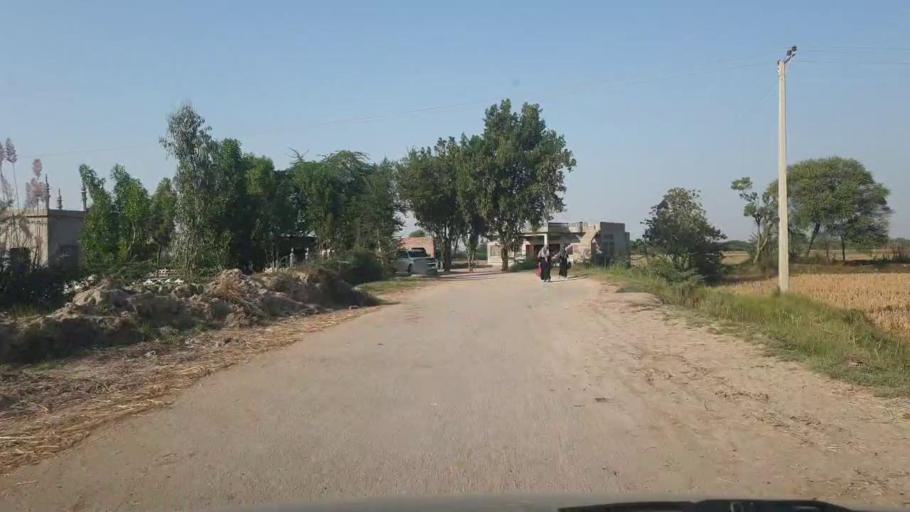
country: PK
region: Sindh
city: Badin
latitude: 24.6569
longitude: 68.8112
